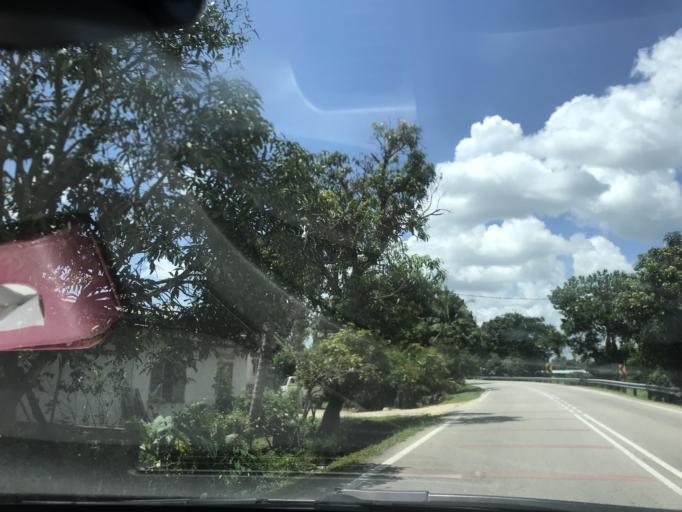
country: MY
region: Kelantan
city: Tumpat
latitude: 6.1975
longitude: 102.1317
